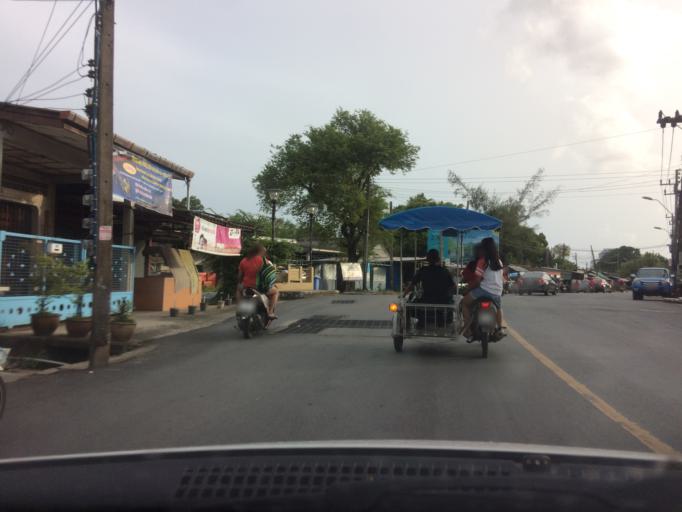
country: TH
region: Phuket
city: Ban Talat Yai
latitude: 7.8849
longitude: 98.4038
